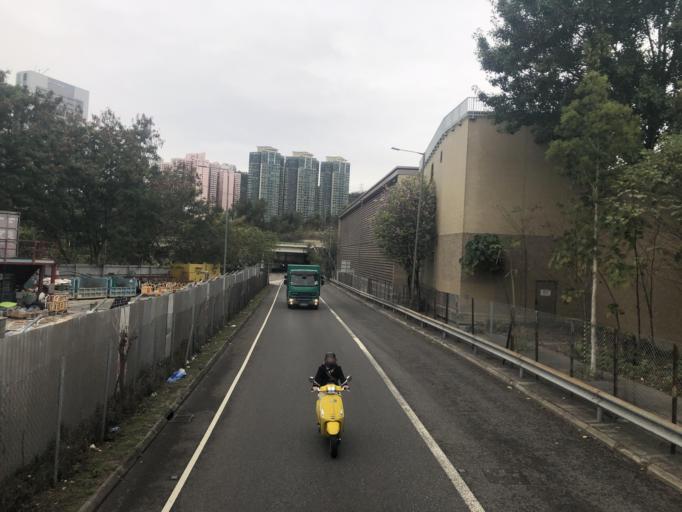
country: HK
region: Sham Shui Po
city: Sham Shui Po
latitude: 22.3363
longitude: 114.1357
